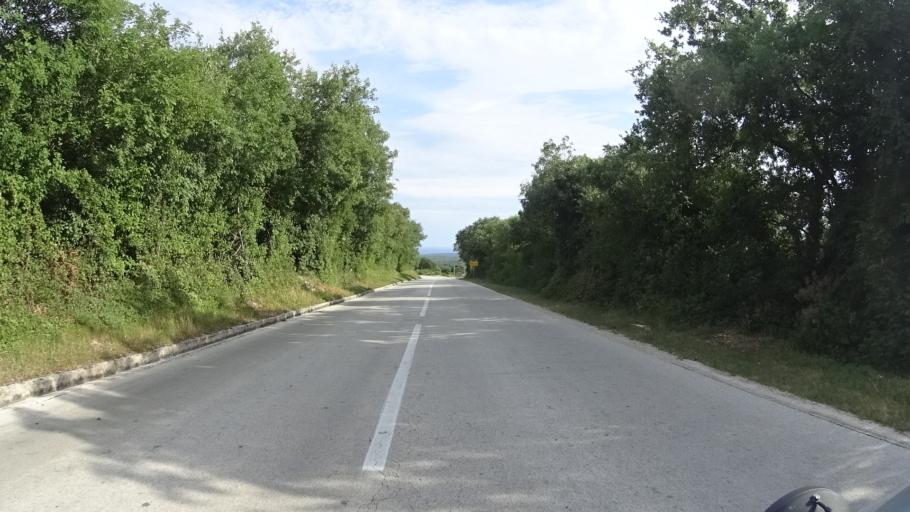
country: HR
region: Istarska
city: Rasa
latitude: 45.0386
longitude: 14.0791
